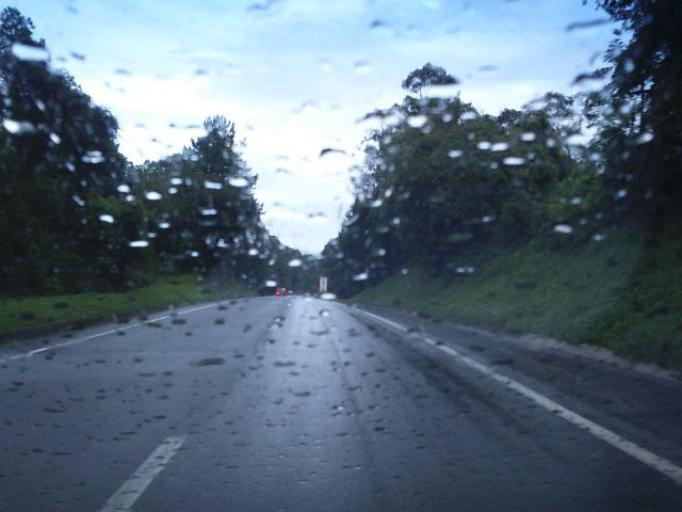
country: BR
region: Parana
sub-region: Sao Jose Dos Pinhais
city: Sao Jose dos Pinhais
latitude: -25.8538
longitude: -49.0225
